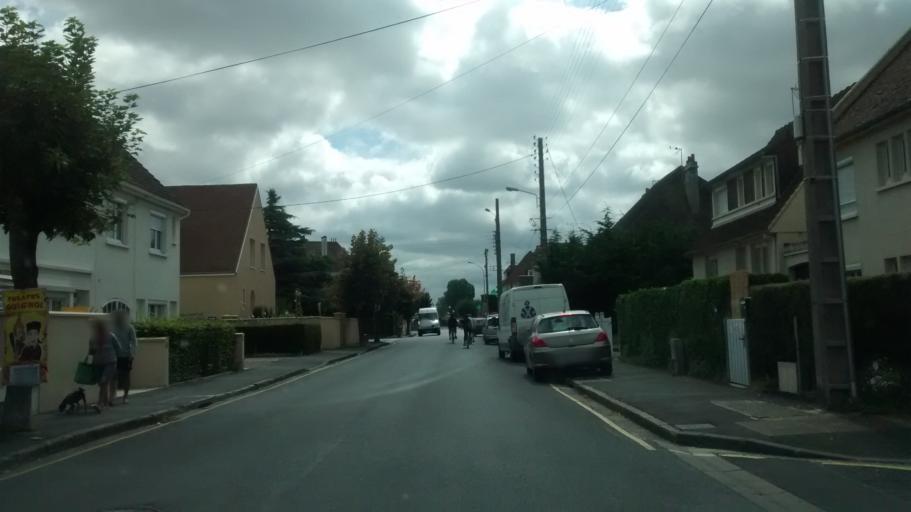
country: FR
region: Lower Normandy
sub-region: Departement du Calvados
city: Ouistreham
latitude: 49.2805
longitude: -0.2526
